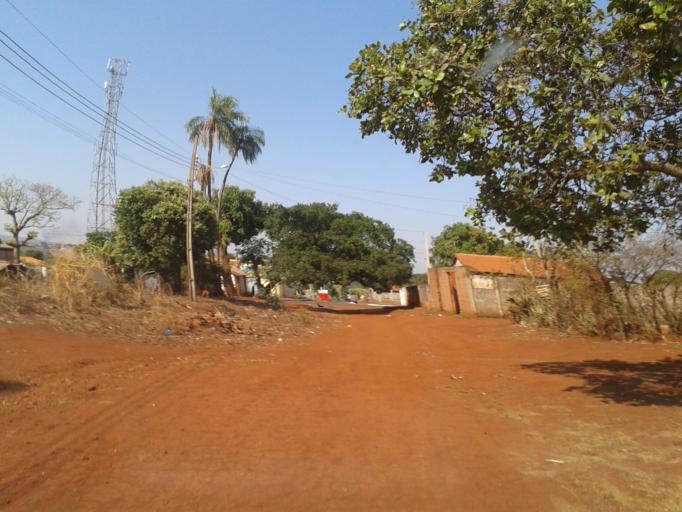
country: BR
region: Minas Gerais
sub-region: Ituiutaba
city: Ituiutaba
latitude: -18.9601
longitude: -49.4796
